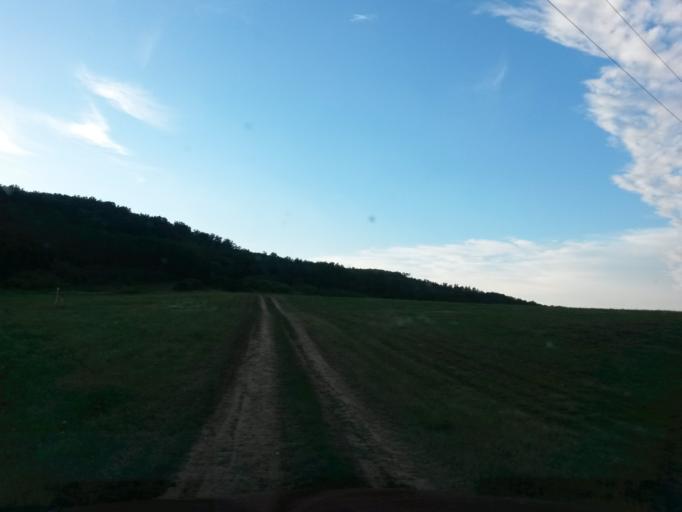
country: SK
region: Banskobystricky
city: Lucenec
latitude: 48.2931
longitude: 19.5060
